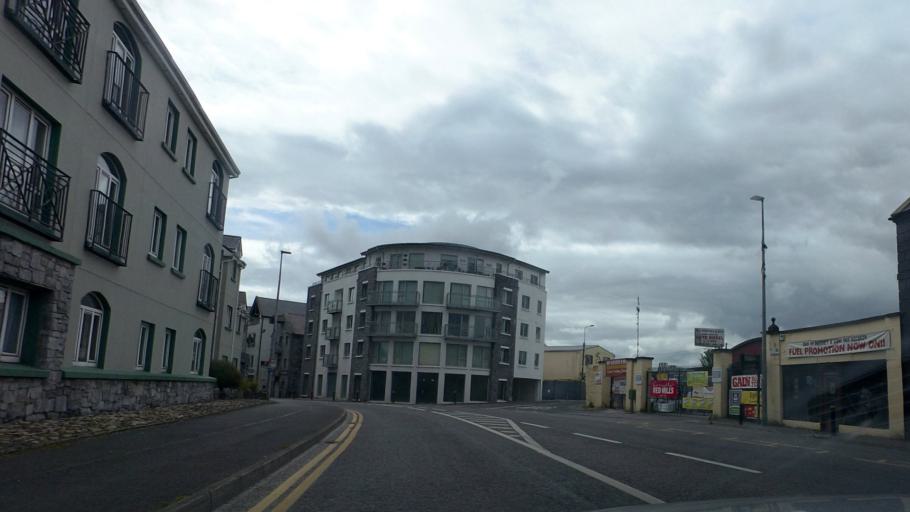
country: IE
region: Munster
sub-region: An Clar
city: Ennis
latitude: 52.8461
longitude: -8.9894
